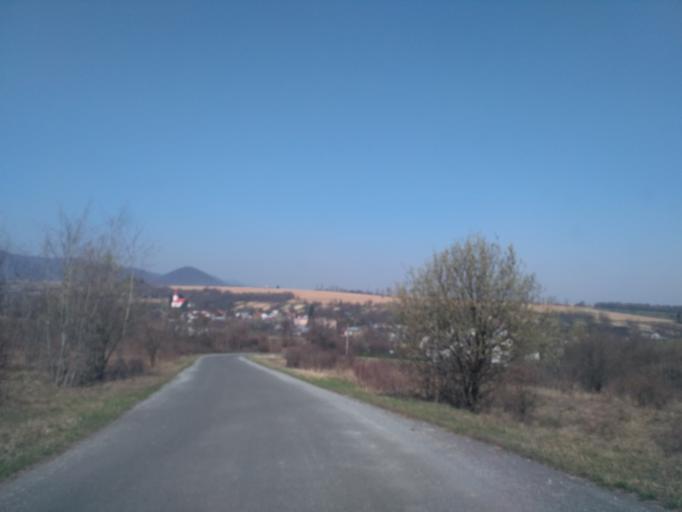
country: SK
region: Presovsky
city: Vranov nad Topl'ou
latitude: 48.8211
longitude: 21.6376
